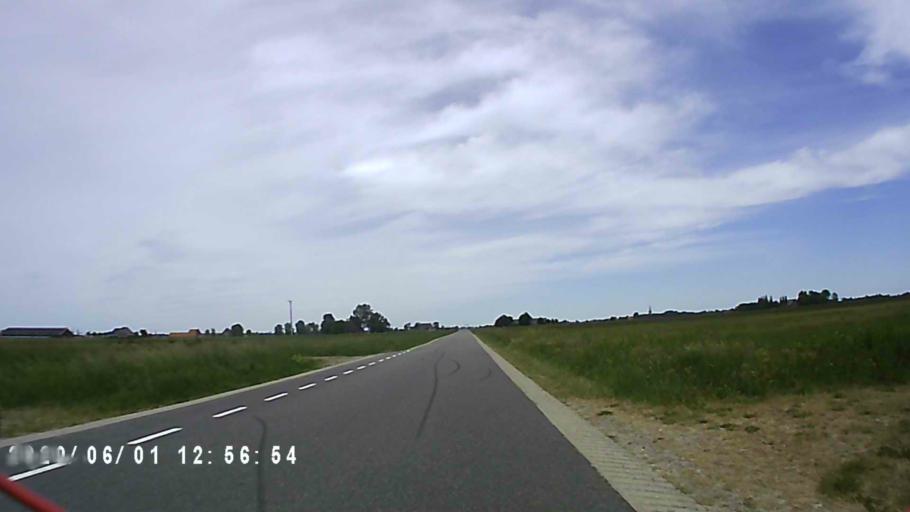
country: NL
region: Friesland
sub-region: Gemeente Franekeradeel
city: Tzum
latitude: 53.1445
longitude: 5.5302
